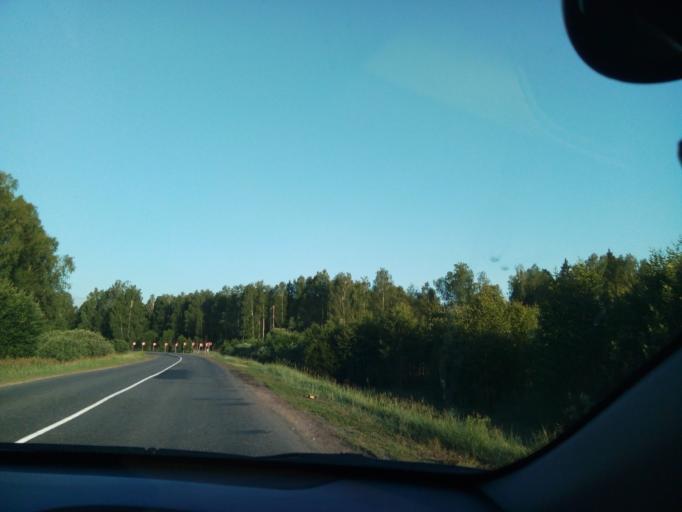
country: RU
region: Nizjnij Novgorod
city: Satis
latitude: 54.9294
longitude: 43.1970
